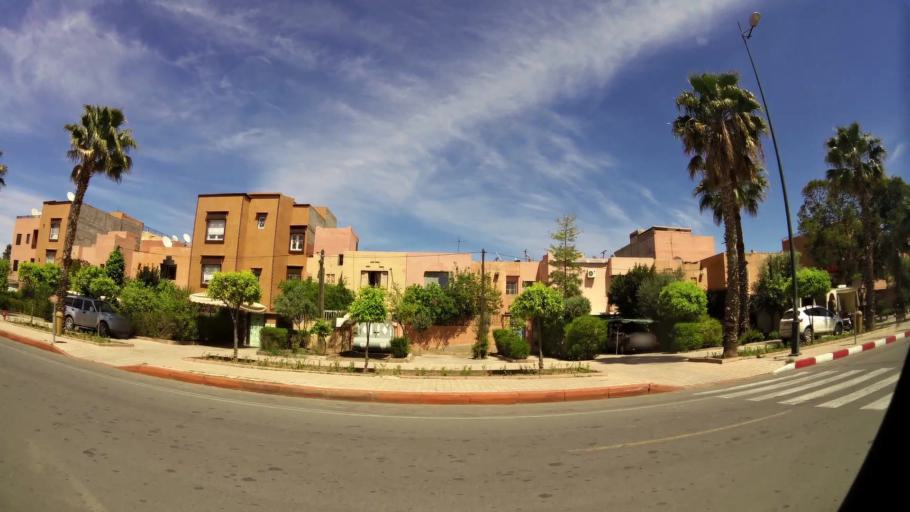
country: MA
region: Marrakech-Tensift-Al Haouz
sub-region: Marrakech
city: Marrakesh
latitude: 31.6043
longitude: -7.9720
